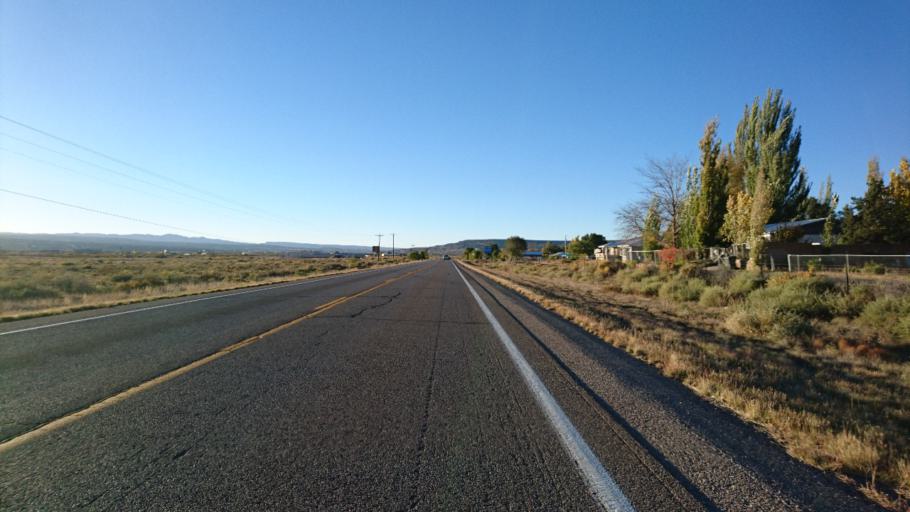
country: US
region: New Mexico
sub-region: Cibola County
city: Grants
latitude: 35.1273
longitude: -107.8053
